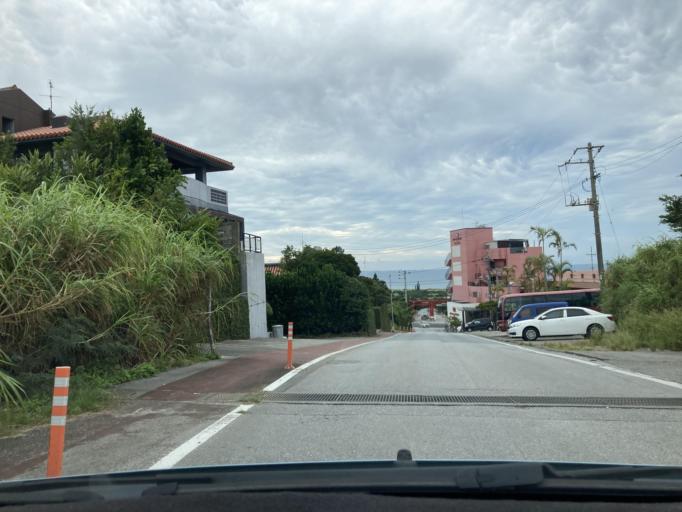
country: JP
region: Okinawa
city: Okinawa
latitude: 26.3866
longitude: 127.7401
